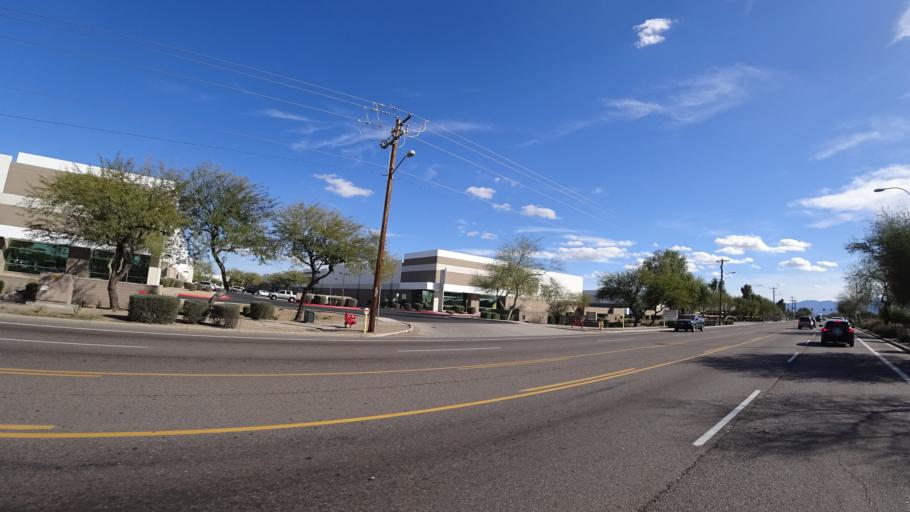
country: US
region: Arizona
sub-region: Maricopa County
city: Tolleson
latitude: 33.4545
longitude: -112.2211
